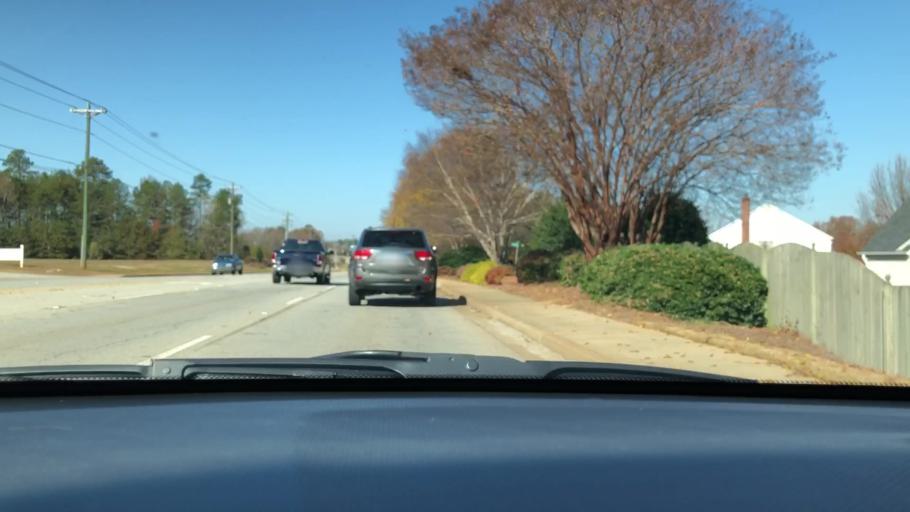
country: US
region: South Carolina
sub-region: Greenville County
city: Five Forks
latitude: 34.8156
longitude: -82.2469
